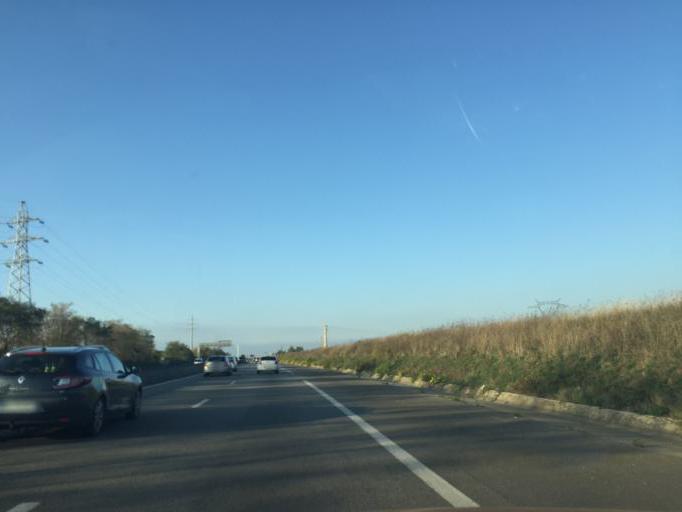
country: FR
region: Rhone-Alpes
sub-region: Departement de la Drome
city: Malissard
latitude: 44.9299
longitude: 4.9456
